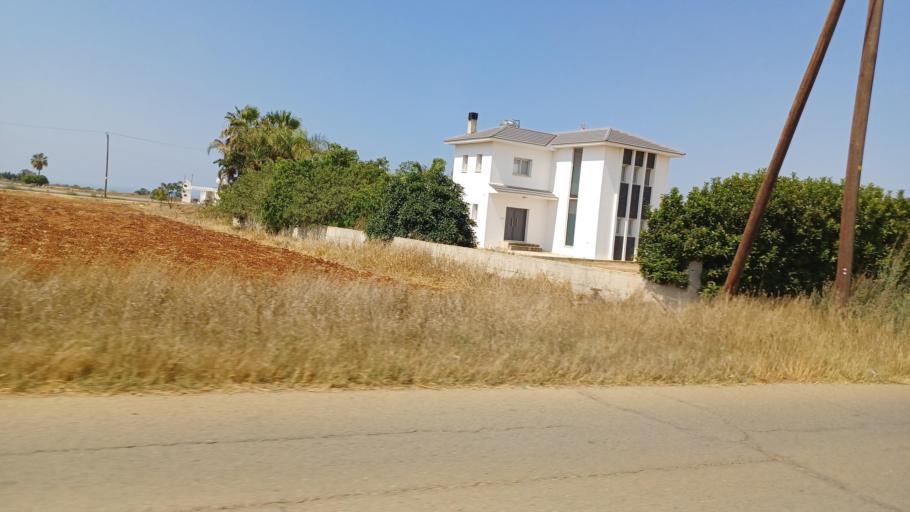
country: CY
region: Ammochostos
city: Avgorou
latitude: 34.9819
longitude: 33.8250
